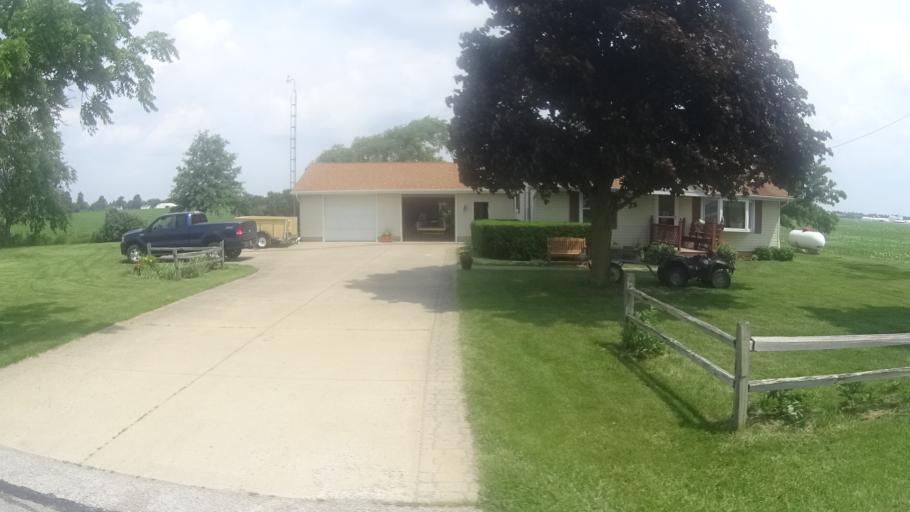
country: US
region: Ohio
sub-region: Huron County
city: Monroeville
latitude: 41.3238
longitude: -82.7141
